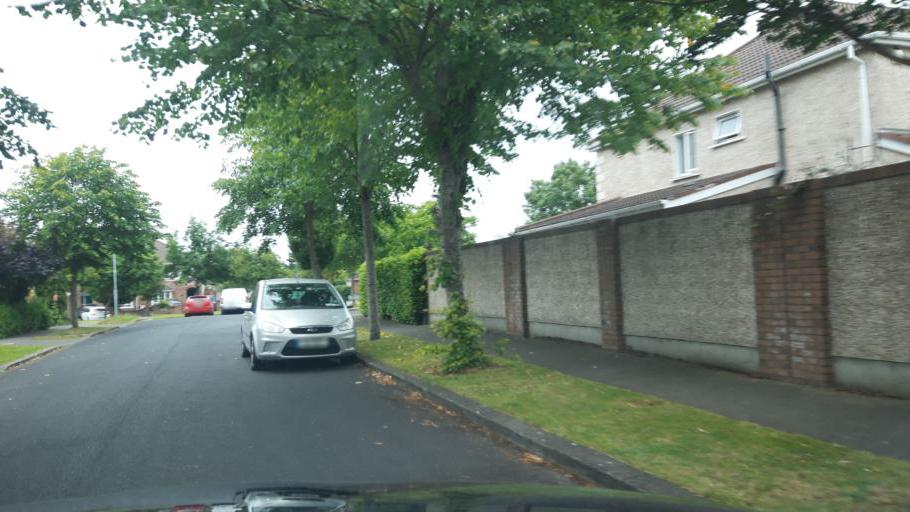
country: IE
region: Leinster
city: Hartstown
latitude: 53.4041
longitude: -6.4160
